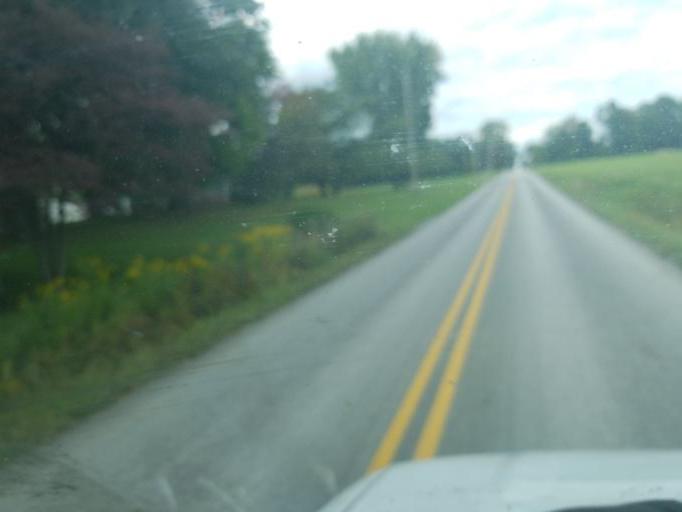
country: US
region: Pennsylvania
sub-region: Mercer County
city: Greenville
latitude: 41.4980
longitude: -80.3381
